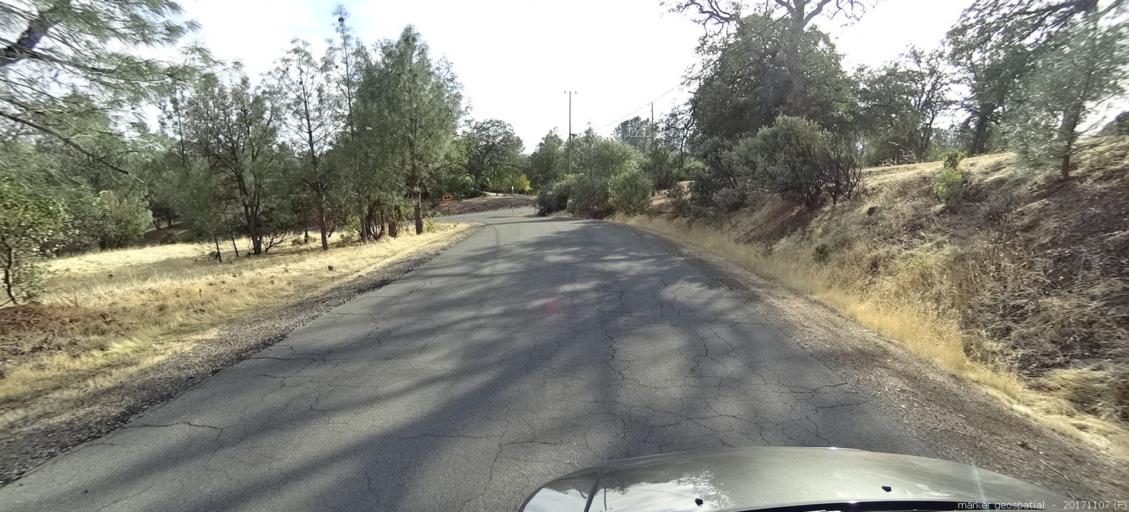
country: US
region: California
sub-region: Shasta County
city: Shasta
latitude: 40.5226
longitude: -122.5002
